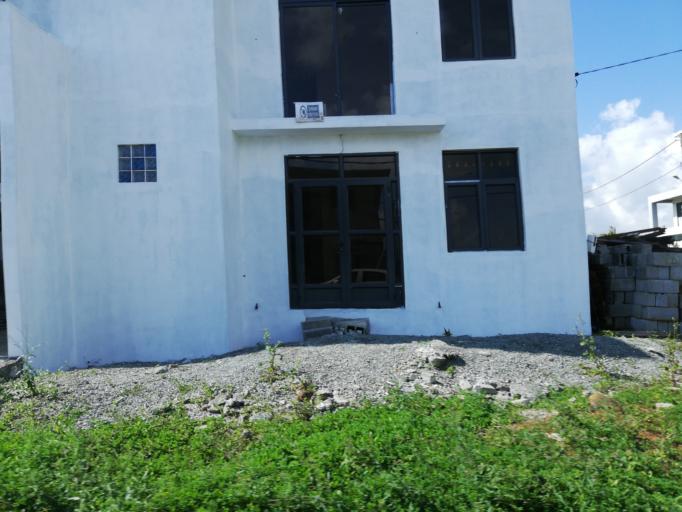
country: MU
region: Moka
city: Verdun
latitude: -20.2133
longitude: 57.5473
